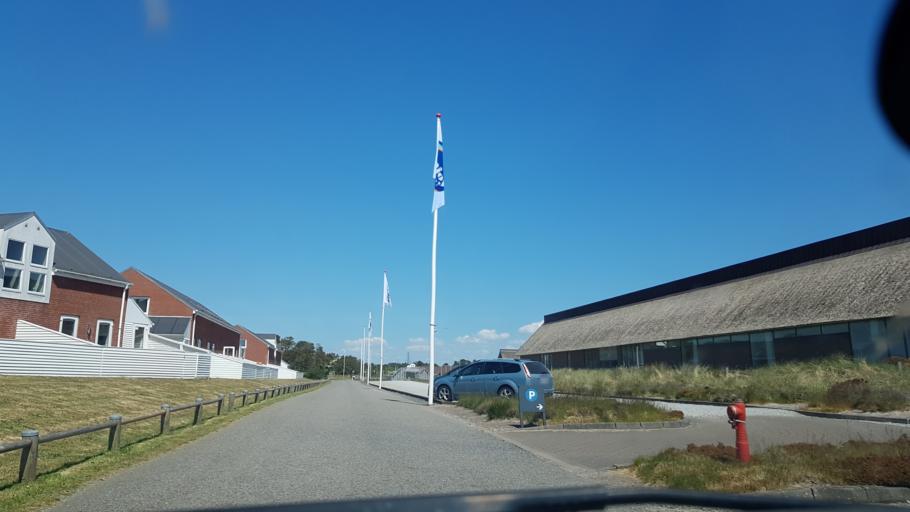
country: DE
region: Schleswig-Holstein
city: List
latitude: 55.0851
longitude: 8.5511
